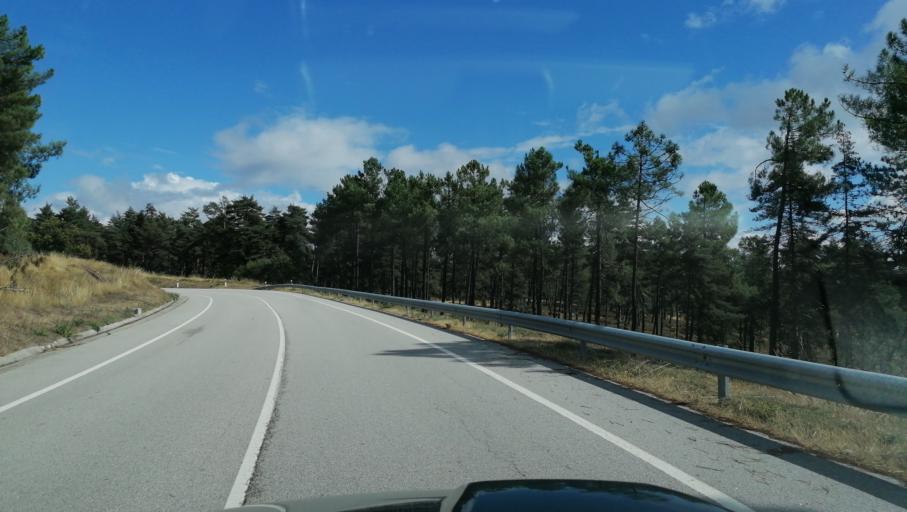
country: PT
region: Vila Real
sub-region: Vila Pouca de Aguiar
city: Vila Pouca de Aguiar
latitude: 41.5195
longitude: -7.5948
